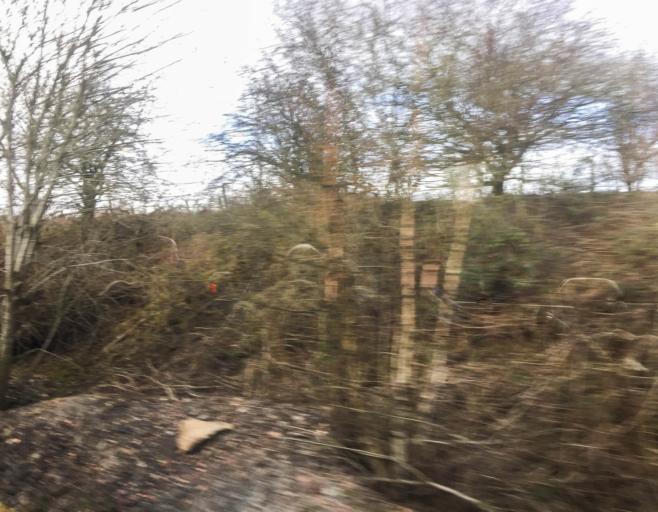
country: GB
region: Scotland
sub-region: North Lanarkshire
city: Wishaw
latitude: 55.7605
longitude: -3.9009
